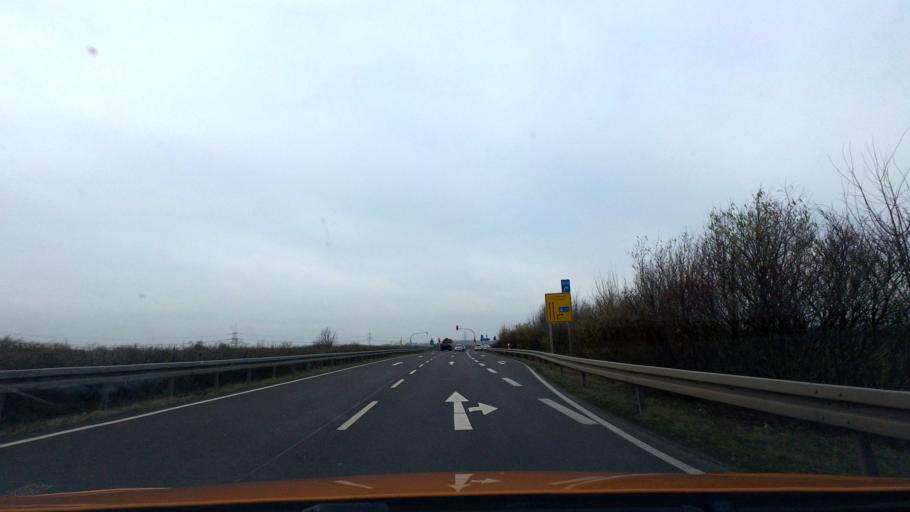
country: DE
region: Saxony-Anhalt
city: Diesdorf
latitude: 52.1428
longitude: 11.5448
